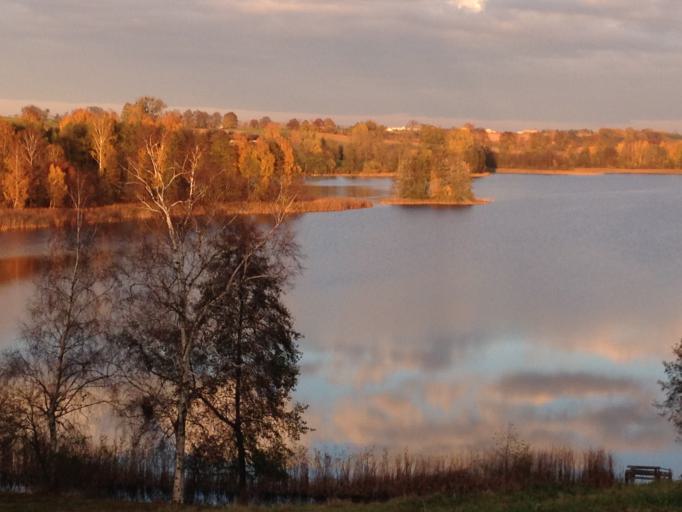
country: PL
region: Kujawsko-Pomorskie
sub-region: Powiat brodnicki
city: Brzozie
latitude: 53.3044
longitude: 19.5912
